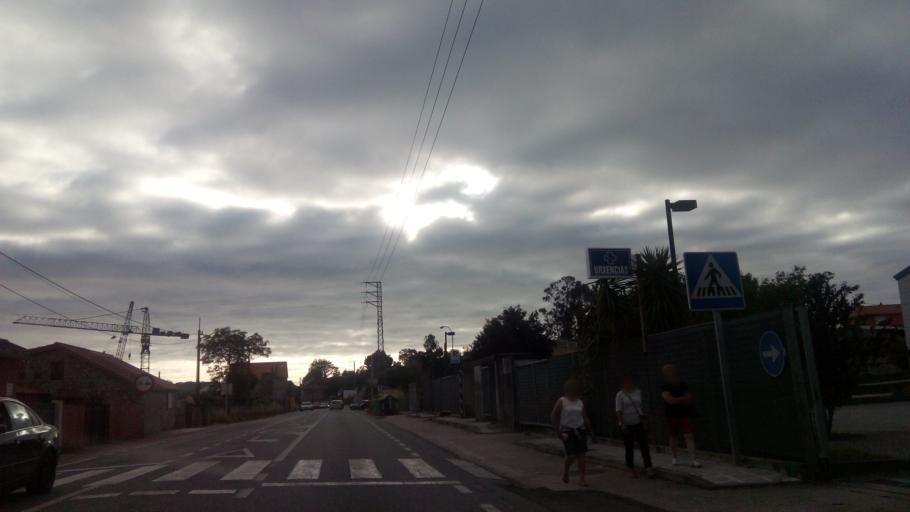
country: ES
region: Galicia
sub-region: Provincia de Pontevedra
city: Nigran
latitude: 42.1146
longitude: -8.8006
